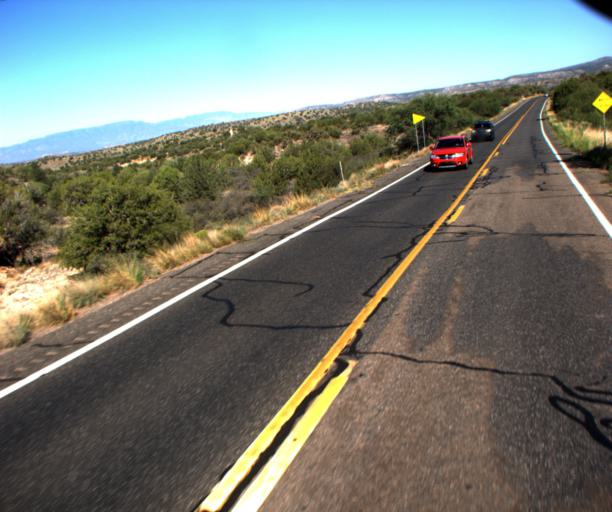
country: US
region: Arizona
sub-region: Yavapai County
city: Lake Montezuma
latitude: 34.7001
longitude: -111.7645
